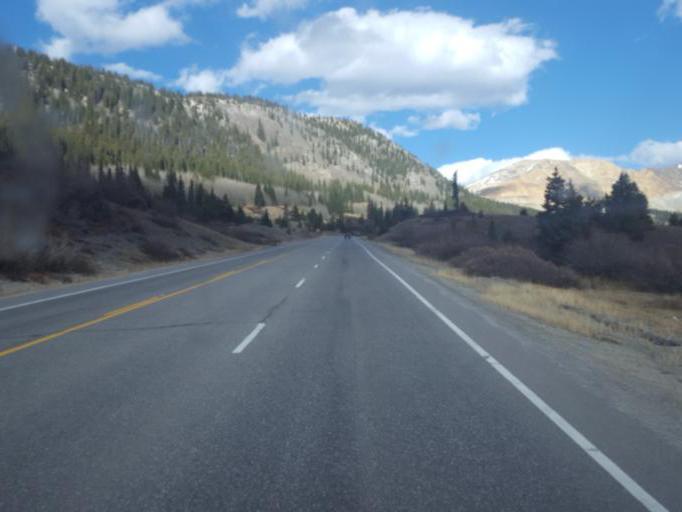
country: US
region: Colorado
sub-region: Lake County
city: Leadville
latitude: 39.3571
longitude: -106.2106
